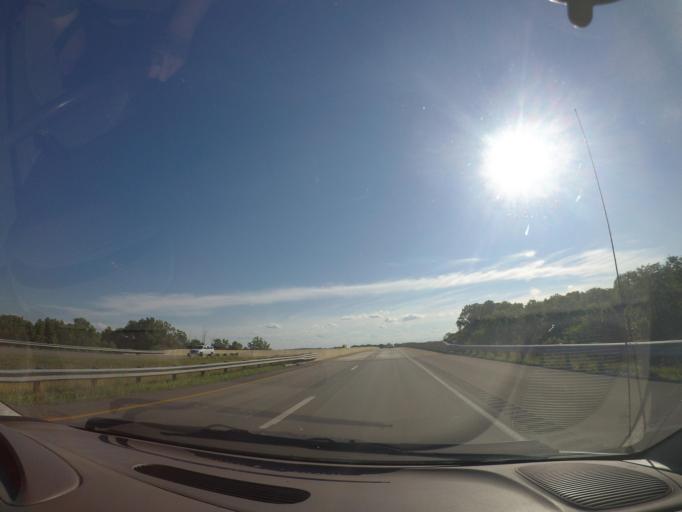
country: US
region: Ohio
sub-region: Henry County
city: Liberty Center
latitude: 41.4205
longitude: -84.0322
